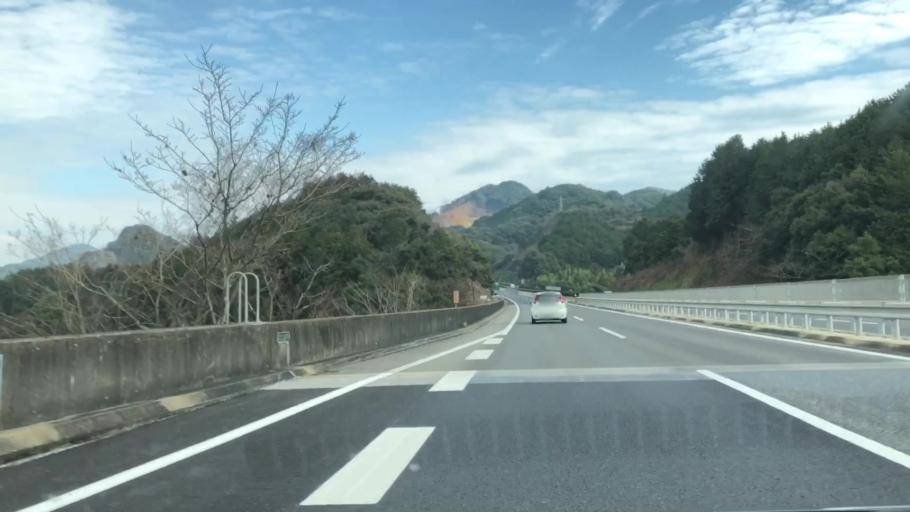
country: JP
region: Saga Prefecture
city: Takeocho-takeo
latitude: 33.1607
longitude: 130.0209
